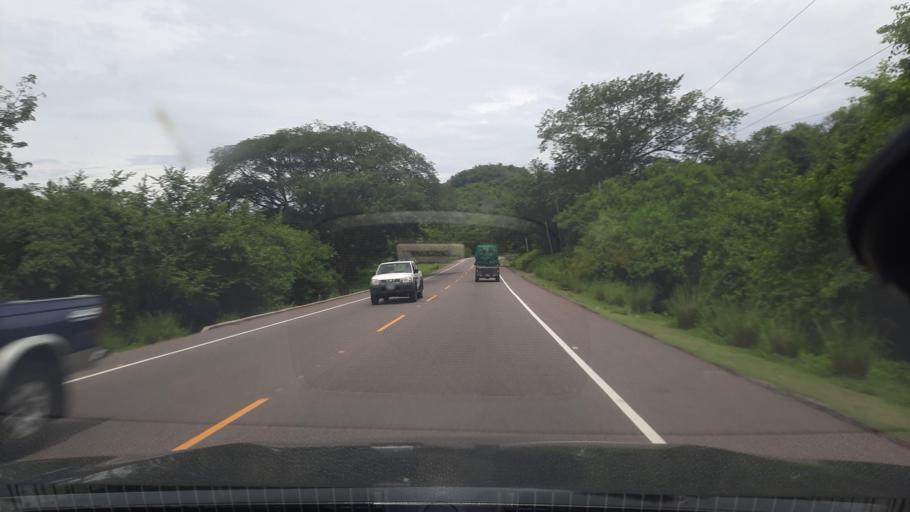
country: HN
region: Valle
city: Langue
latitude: 13.5722
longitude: -87.6740
